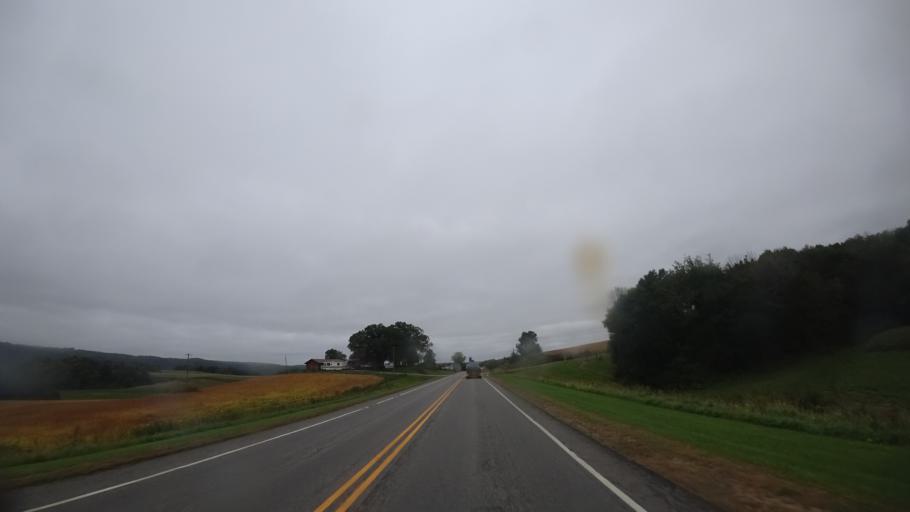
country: US
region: Wisconsin
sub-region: Crawford County
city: Prairie du Chien
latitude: 43.0290
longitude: -91.0159
